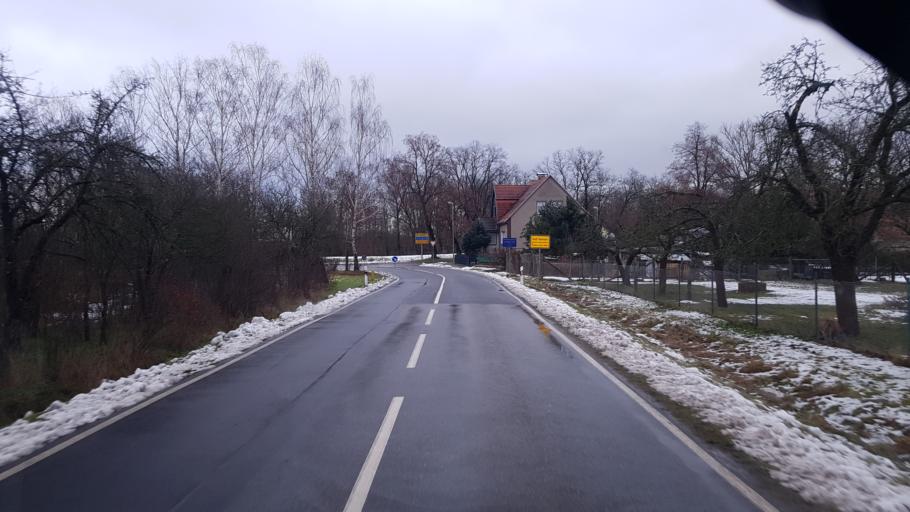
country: DE
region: Brandenburg
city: Schenkendobern
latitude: 51.8858
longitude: 14.6516
